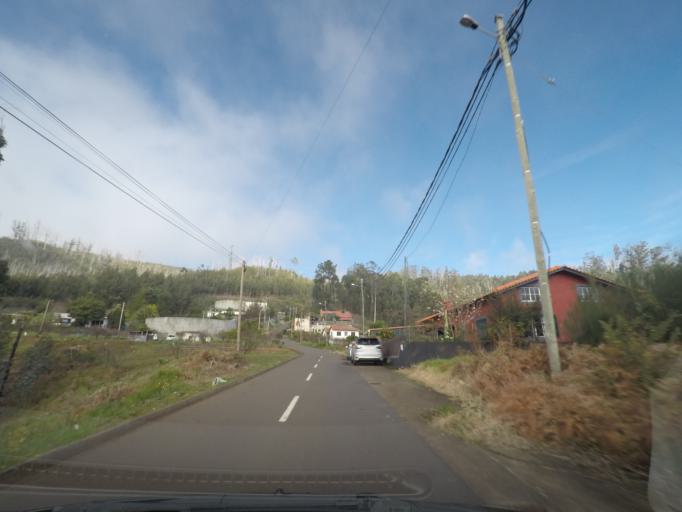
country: PT
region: Madeira
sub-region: Calheta
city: Estreito da Calheta
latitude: 32.7490
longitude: -17.1884
